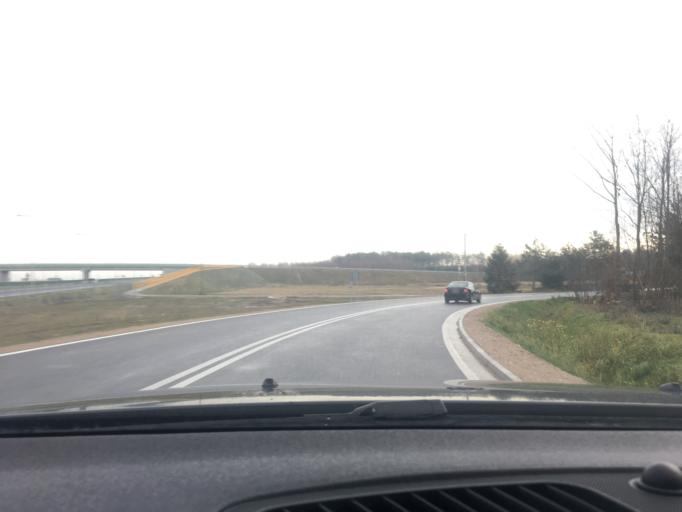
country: PL
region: Swietokrzyskie
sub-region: Powiat jedrzejowski
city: Jedrzejow
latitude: 50.6891
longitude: 20.3672
